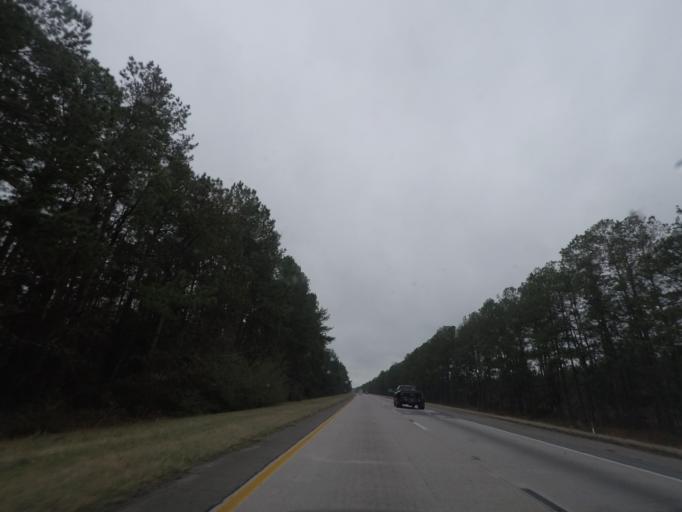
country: US
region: South Carolina
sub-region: Dorchester County
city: Saint George
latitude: 33.0736
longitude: -80.6583
